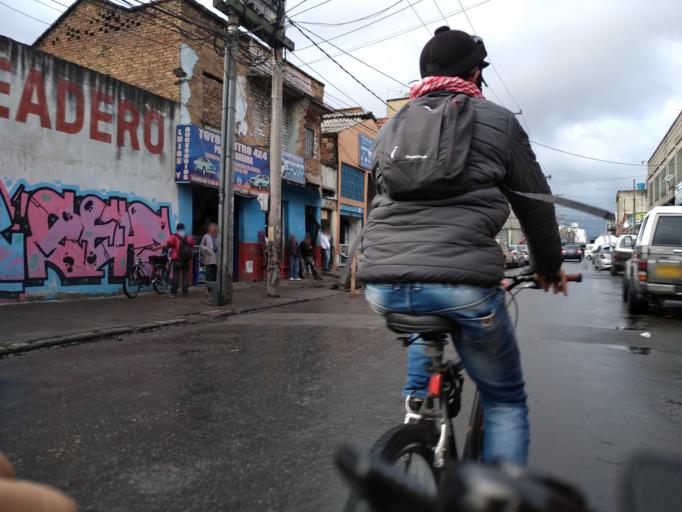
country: CO
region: Bogota D.C.
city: Bogota
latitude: 4.6015
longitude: -74.0855
